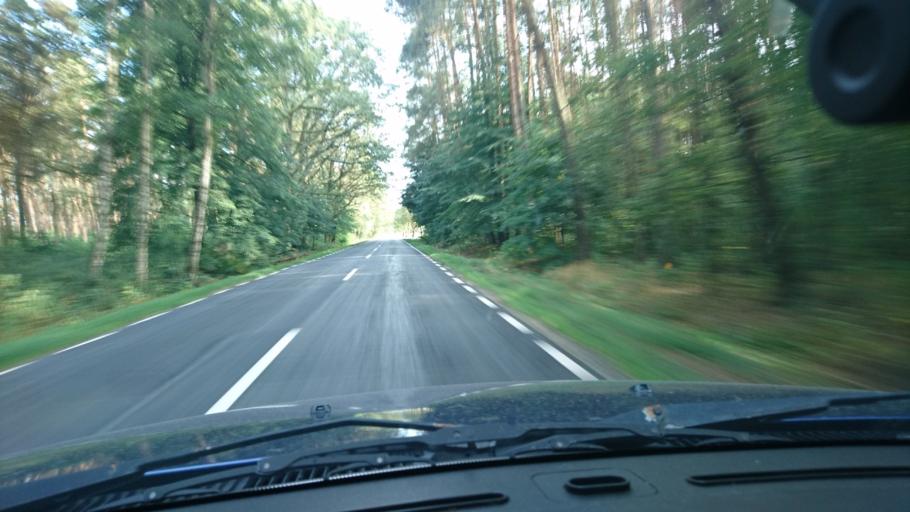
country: PL
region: Greater Poland Voivodeship
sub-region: Powiat krotoszynski
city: Sulmierzyce
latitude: 51.6251
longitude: 17.4981
